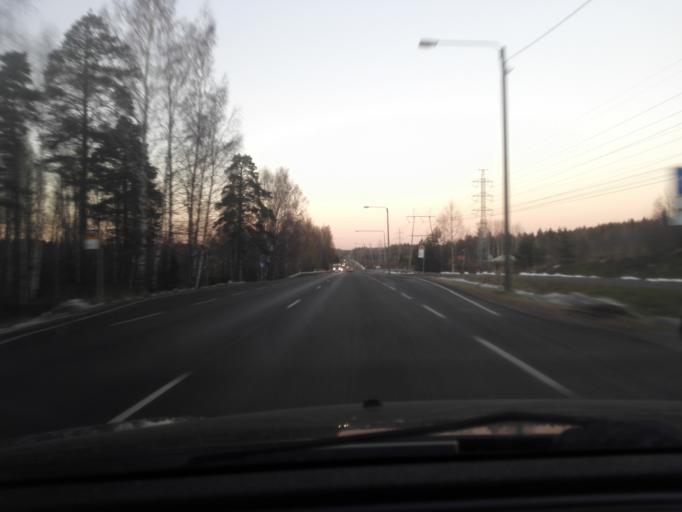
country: FI
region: Uusimaa
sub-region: Helsinki
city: Vantaa
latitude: 60.3190
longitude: 25.1149
